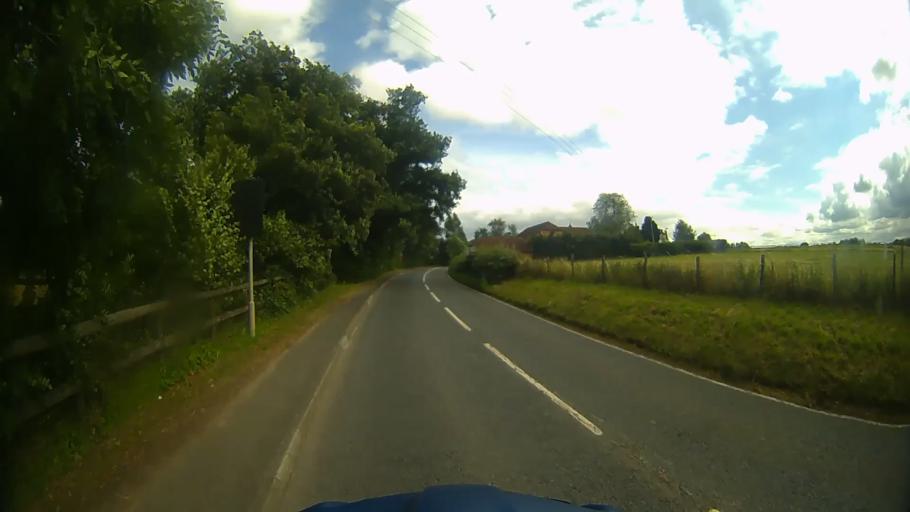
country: GB
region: England
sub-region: Wokingham
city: Barkham
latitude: 51.3964
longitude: -0.8832
